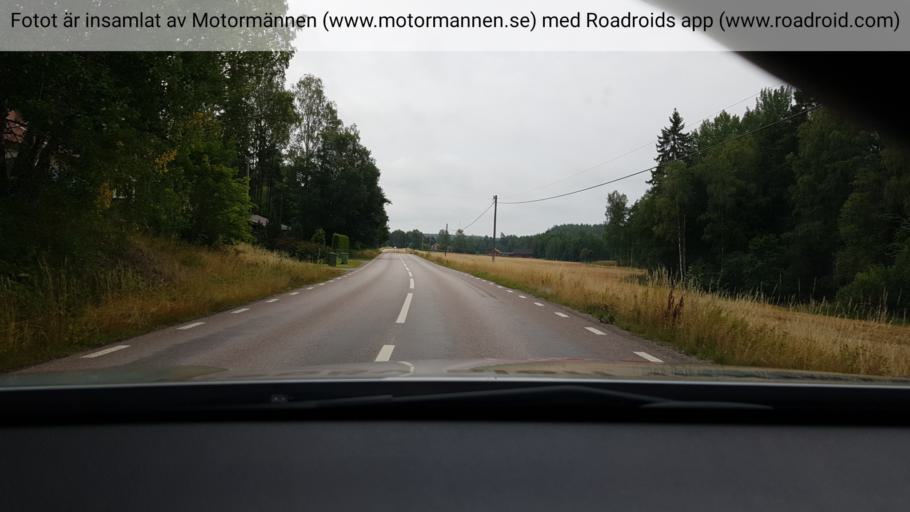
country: SE
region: Soedermanland
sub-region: Strangnas Kommun
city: Mariefred
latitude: 59.2169
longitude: 17.1725
